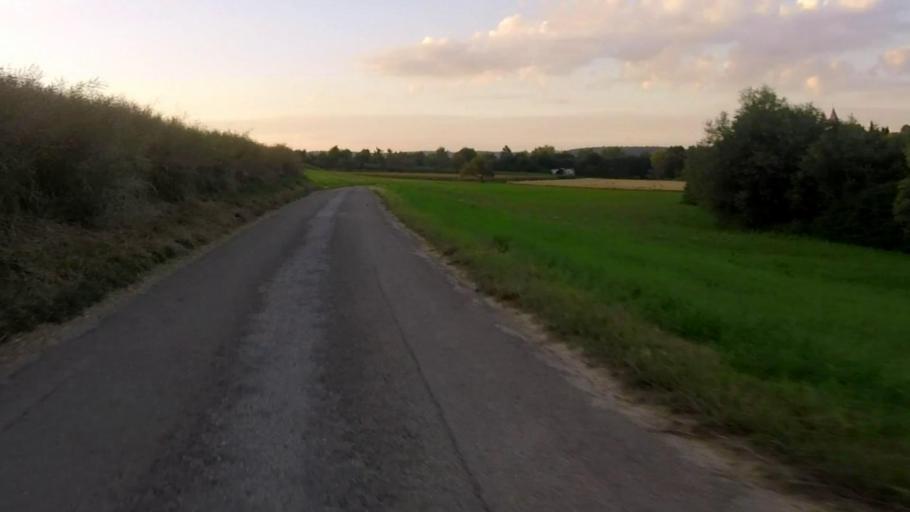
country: DE
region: Baden-Wuerttemberg
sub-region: Regierungsbezirk Stuttgart
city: Aspach
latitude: 48.9603
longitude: 9.3934
